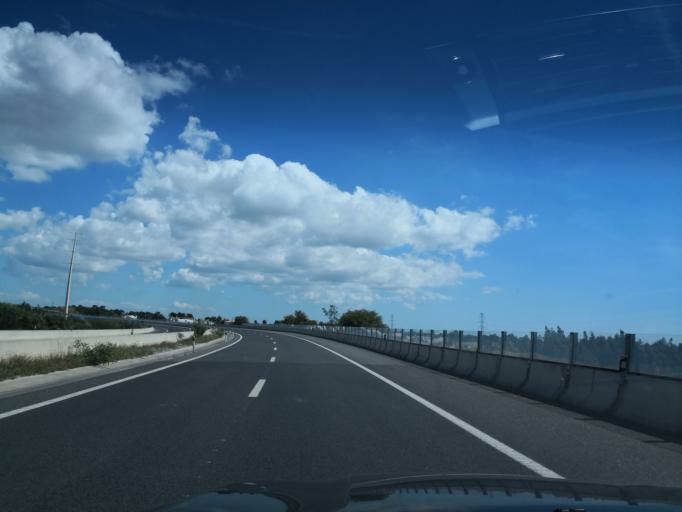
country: PT
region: Setubal
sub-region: Almada
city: Charneca
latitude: 38.6125
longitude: -9.1677
